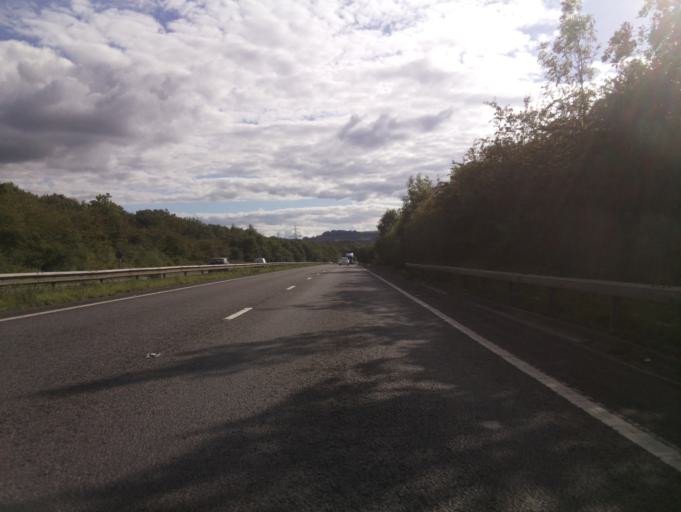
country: GB
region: England
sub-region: Devon
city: Bovey Tracey
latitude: 50.5790
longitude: -3.6381
